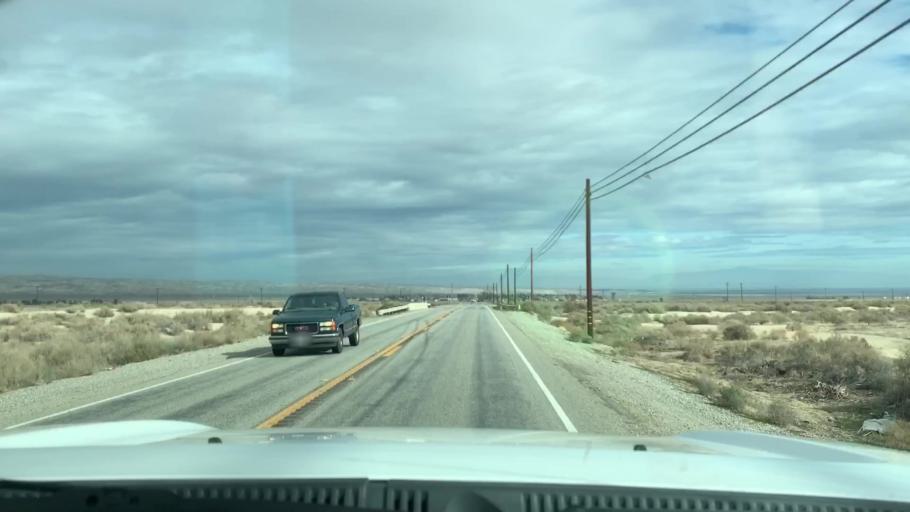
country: US
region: California
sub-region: Kern County
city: Ford City
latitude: 35.1906
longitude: -119.4335
